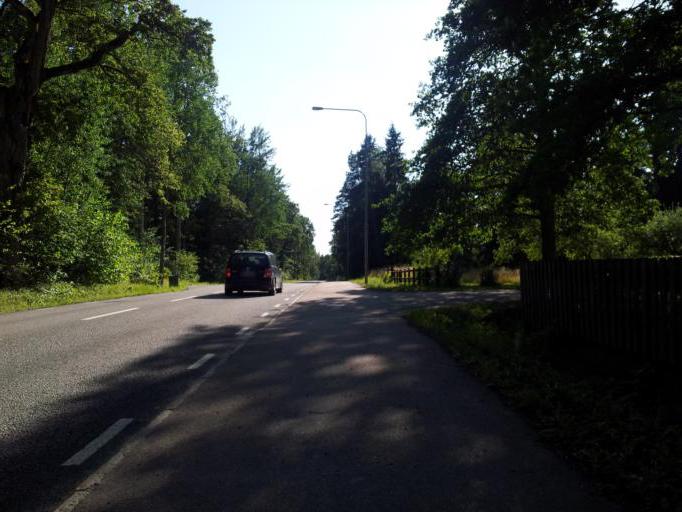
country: SE
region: Uppsala
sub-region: Knivsta Kommun
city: Knivsta
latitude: 59.8674
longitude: 17.9442
